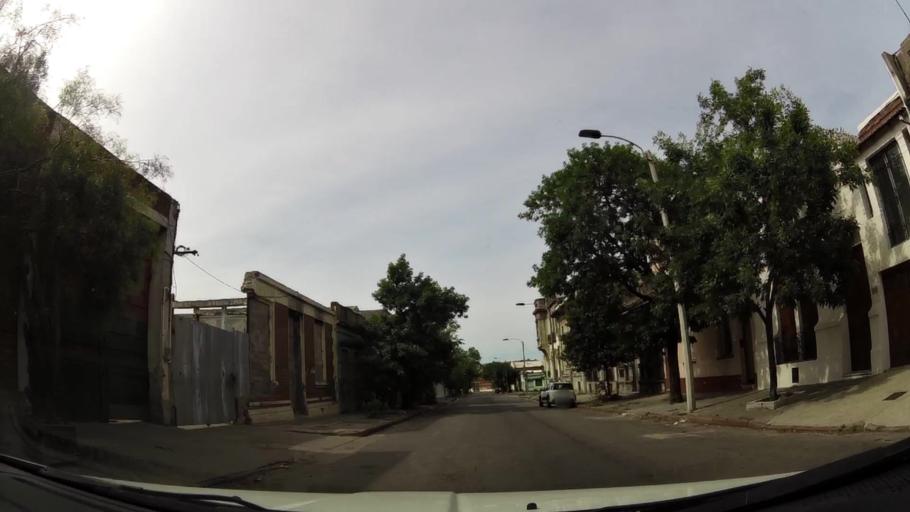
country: UY
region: Montevideo
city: Montevideo
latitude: -34.8774
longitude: -56.1996
